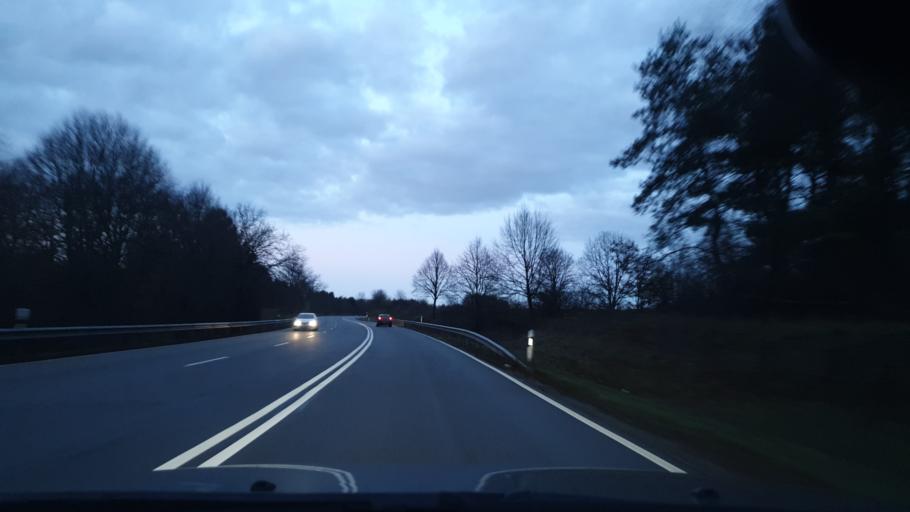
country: DE
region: Rheinland-Pfalz
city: Schopp
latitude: 49.3450
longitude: 7.6787
